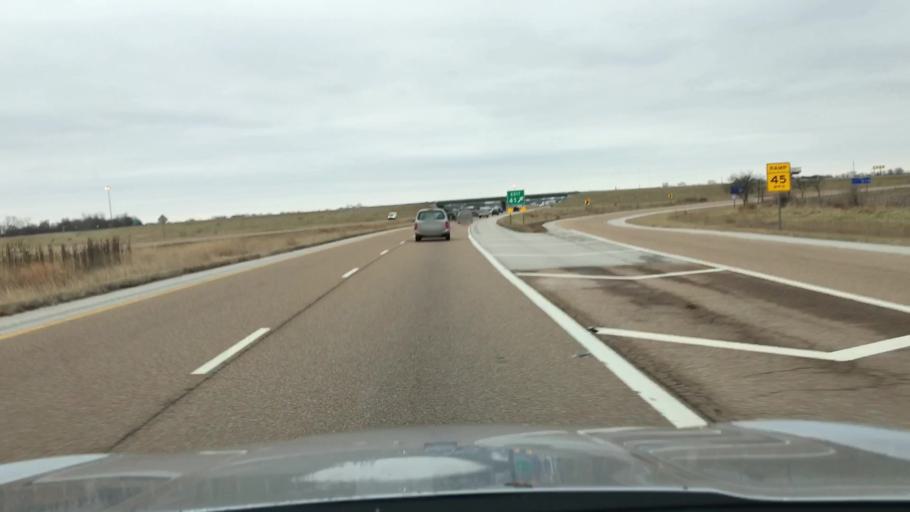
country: US
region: Illinois
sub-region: Macoupin County
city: Staunton
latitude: 39.0249
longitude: -89.7503
